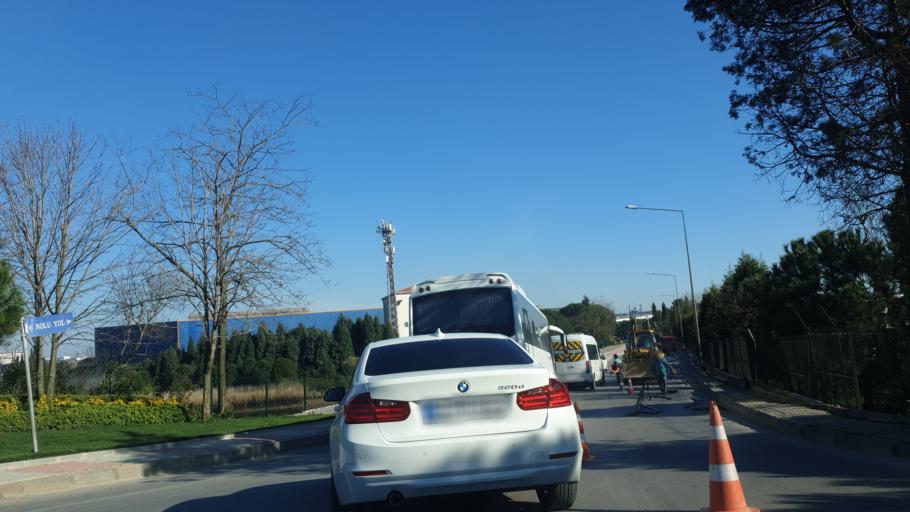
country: TR
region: Istanbul
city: Icmeler
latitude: 40.8801
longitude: 29.3577
